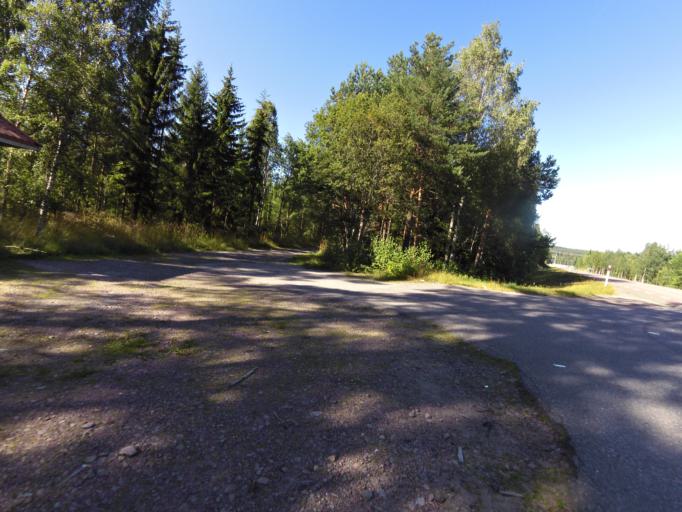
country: SE
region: Gaevleborg
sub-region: Sandvikens Kommun
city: Jarbo
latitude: 60.5625
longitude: 16.4866
